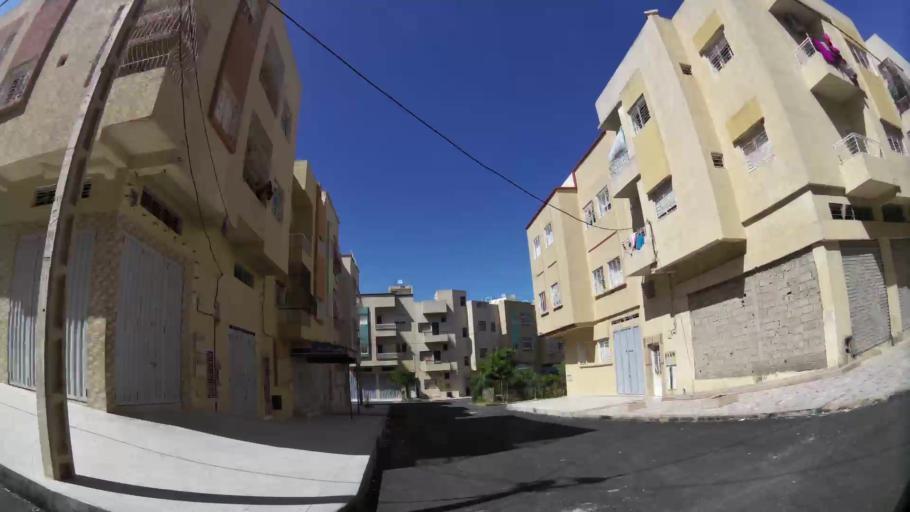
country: MA
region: Fes-Boulemane
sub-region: Fes
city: Fes
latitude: 34.0074
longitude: -5.0328
